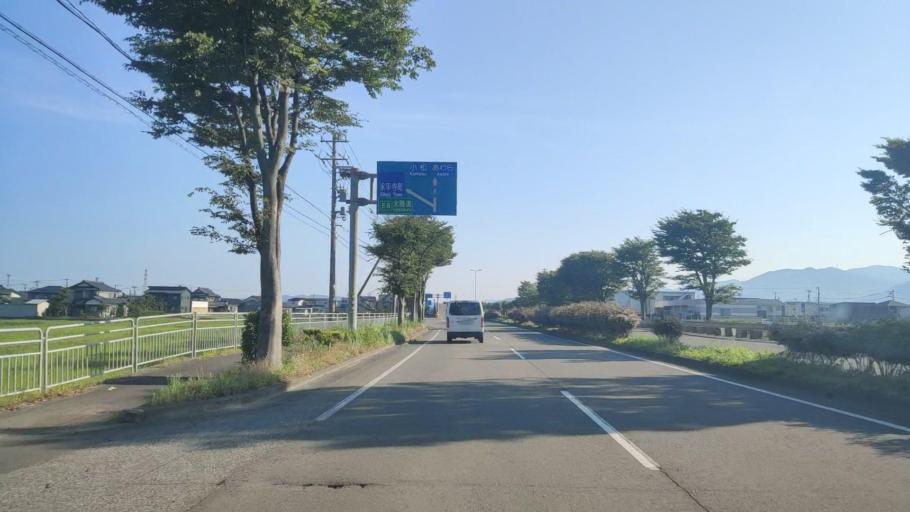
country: JP
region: Fukui
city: Maruoka
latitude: 36.1389
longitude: 136.2633
